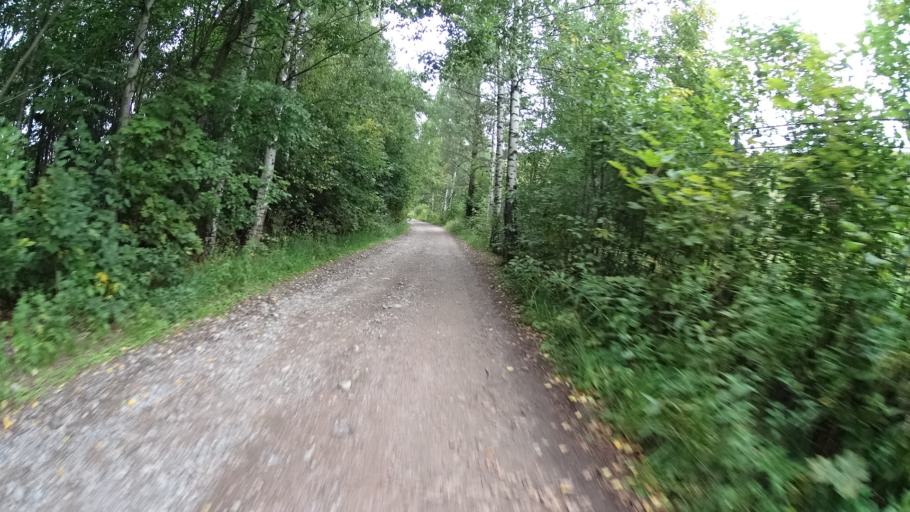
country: FI
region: Uusimaa
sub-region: Helsinki
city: Teekkarikylae
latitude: 60.2768
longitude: 24.8886
